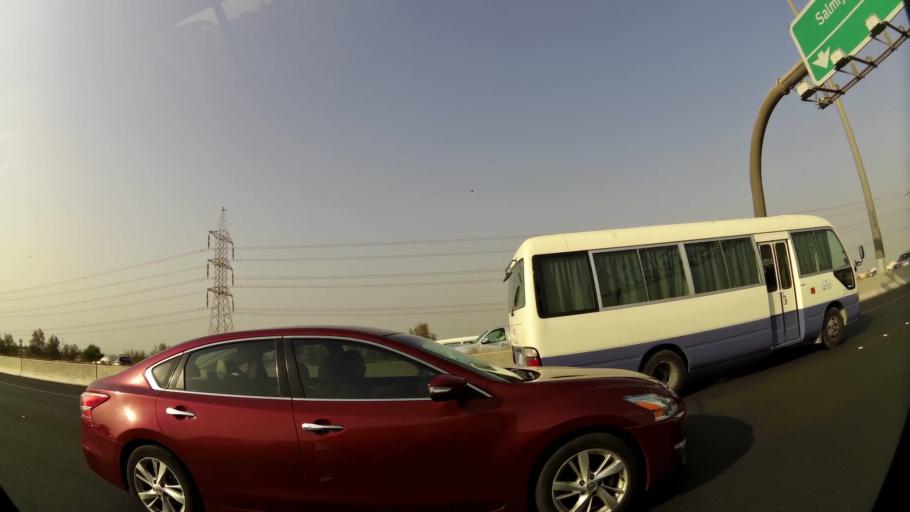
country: KW
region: Al Farwaniyah
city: Al Farwaniyah
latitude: 29.3025
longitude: 47.9591
